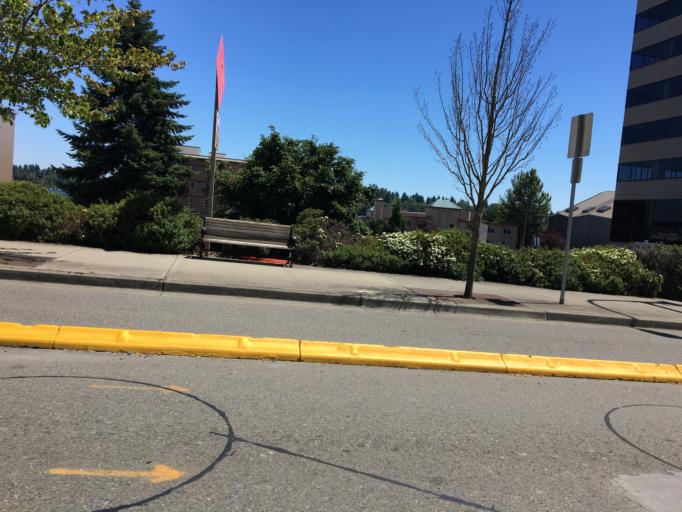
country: US
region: Washington
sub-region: King County
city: Bellevue
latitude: 47.6123
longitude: -122.1936
